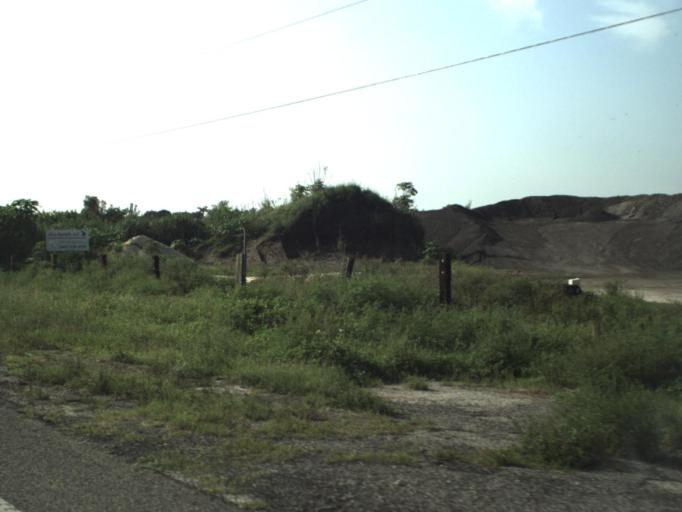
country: US
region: Florida
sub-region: Hendry County
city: Clewiston
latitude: 26.7435
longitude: -80.8859
